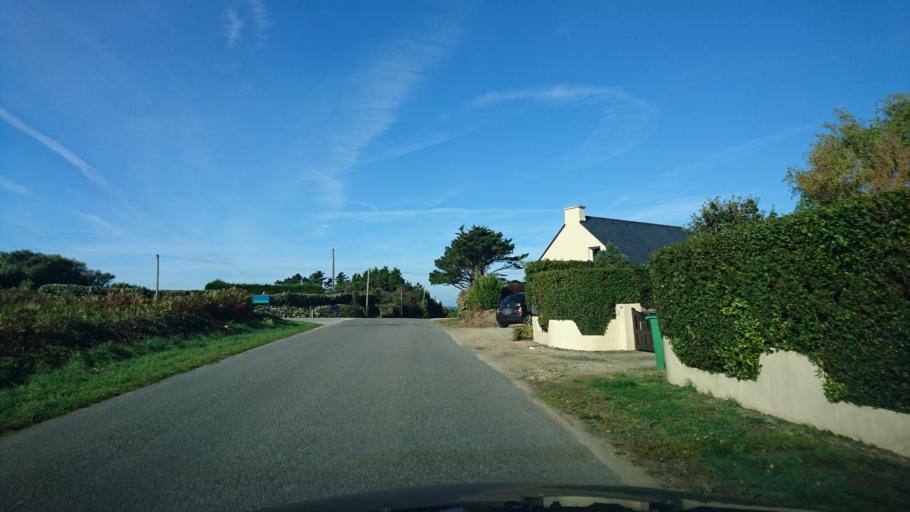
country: FR
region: Brittany
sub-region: Departement du Finistere
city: Lampaul-Plouarzel
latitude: 48.4318
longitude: -4.7682
